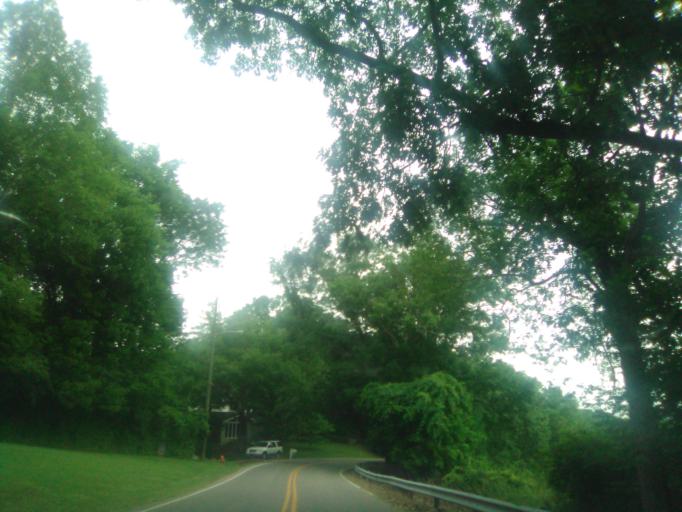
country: US
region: Tennessee
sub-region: Davidson County
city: Belle Meade
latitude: 36.0864
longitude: -86.8946
